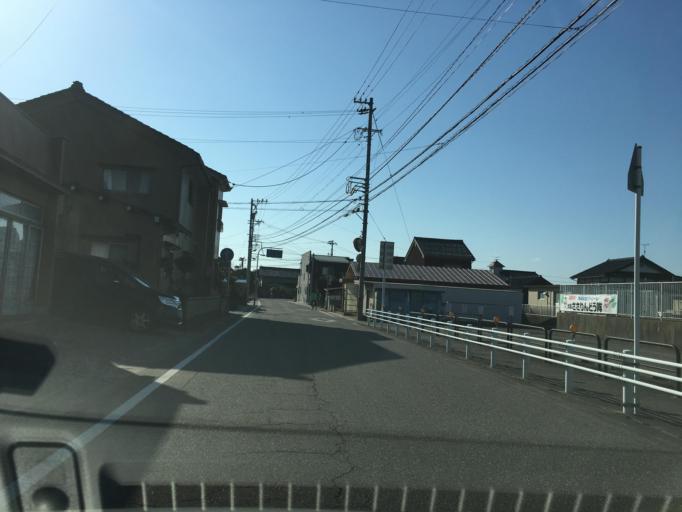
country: JP
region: Toyama
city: Himi
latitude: 36.8209
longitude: 137.0238
